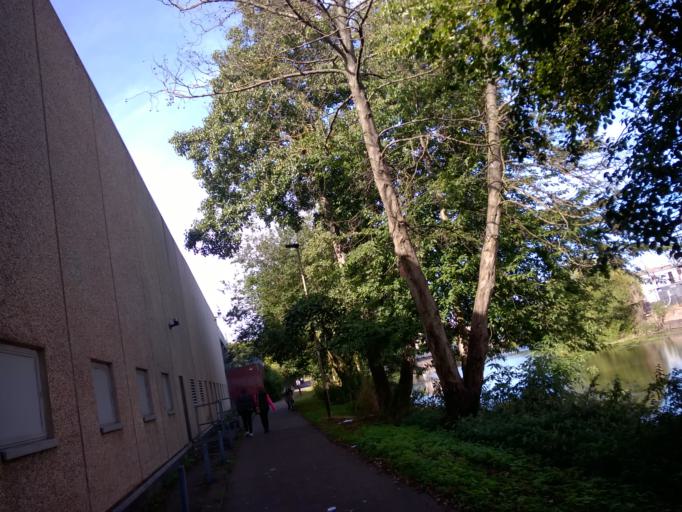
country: GB
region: England
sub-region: City of Leicester
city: Leicester
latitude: 52.6365
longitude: -1.1453
